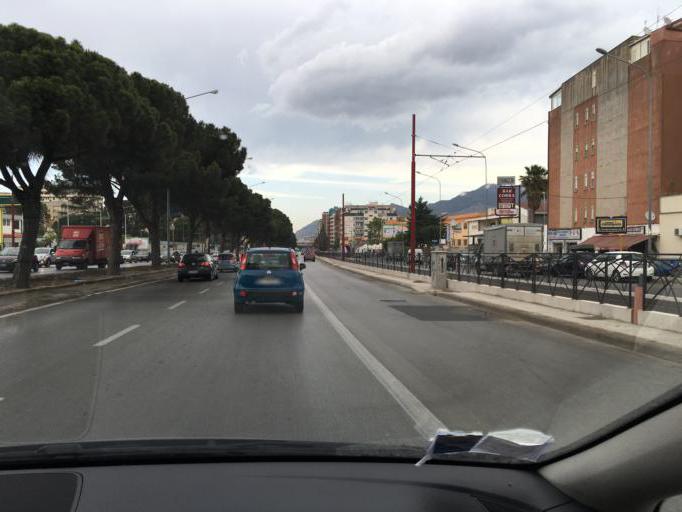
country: IT
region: Sicily
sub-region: Palermo
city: Palermo
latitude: 38.1197
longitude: 13.3289
